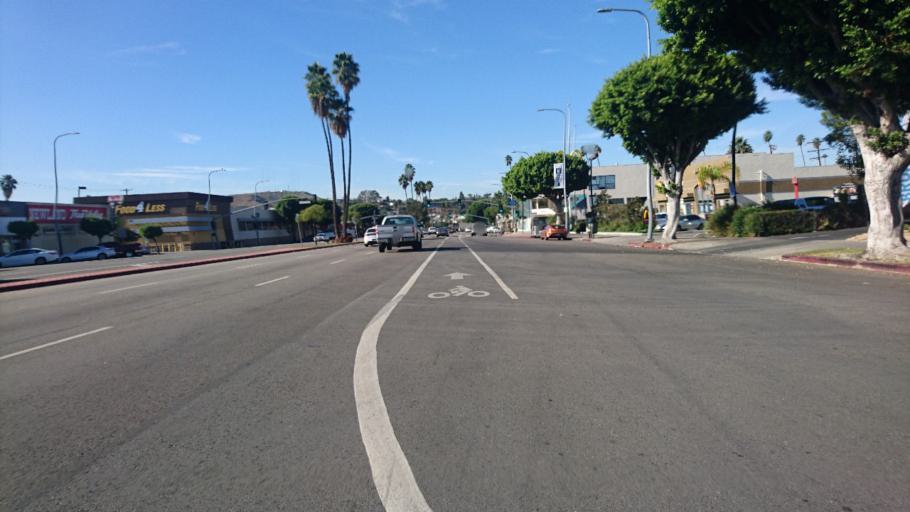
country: US
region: California
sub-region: Los Angeles County
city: South Pasadena
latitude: 34.0877
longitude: -118.1750
